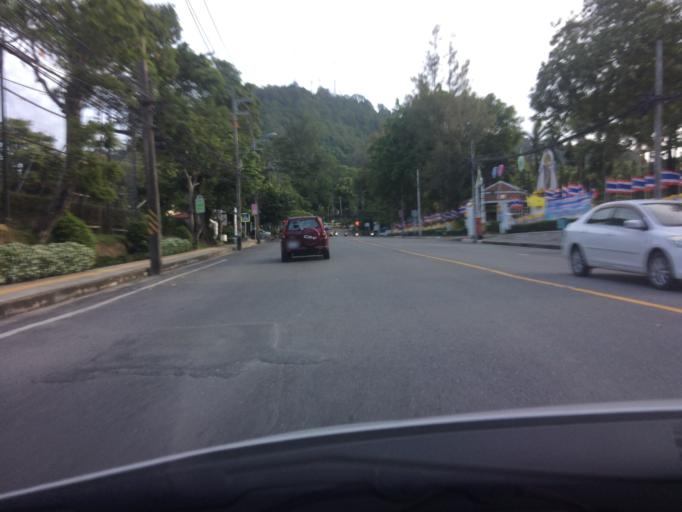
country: TH
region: Phuket
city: Phuket
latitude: 7.8892
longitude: 98.3979
